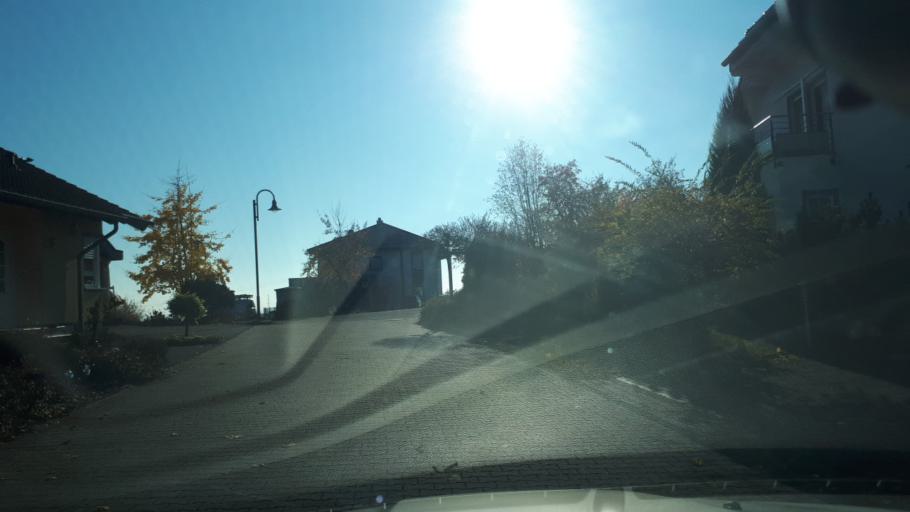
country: DE
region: Rheinland-Pfalz
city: Illerich
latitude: 50.1985
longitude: 7.1854
